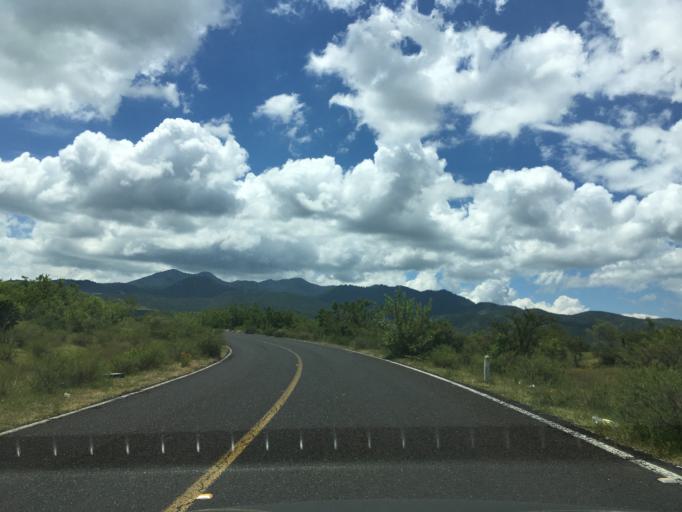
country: MX
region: Mexico
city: Huaniqueo de Morales
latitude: 19.7994
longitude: -101.4569
